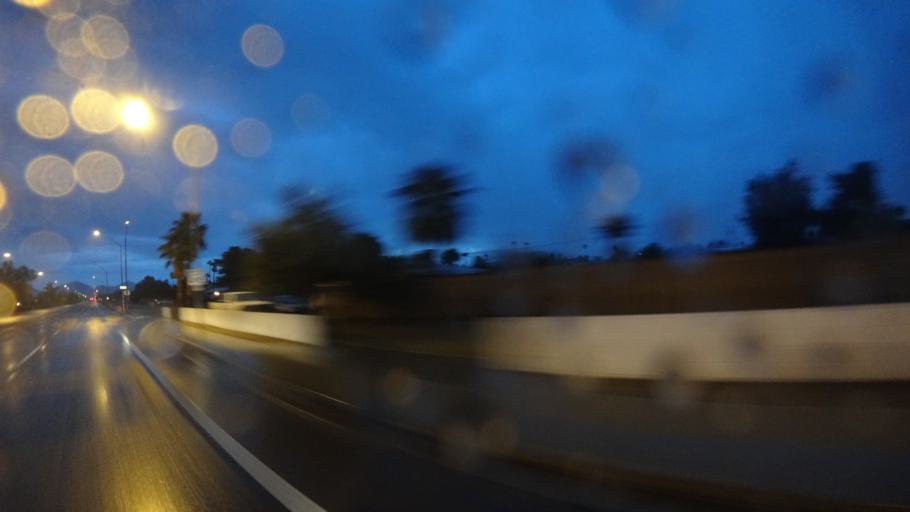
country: US
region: Arizona
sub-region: Maricopa County
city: Paradise Valley
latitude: 33.6552
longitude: -111.9911
